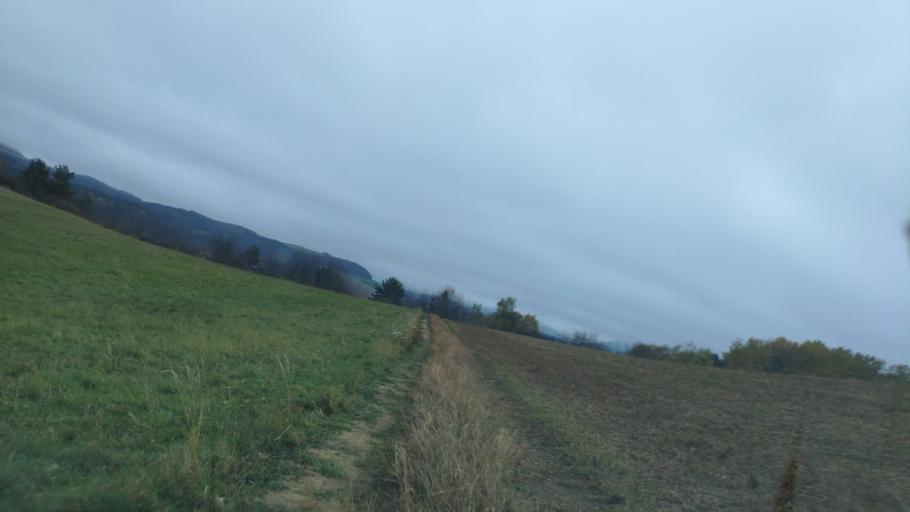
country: SK
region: Presovsky
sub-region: Okres Presov
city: Presov
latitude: 48.9308
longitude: 21.0944
